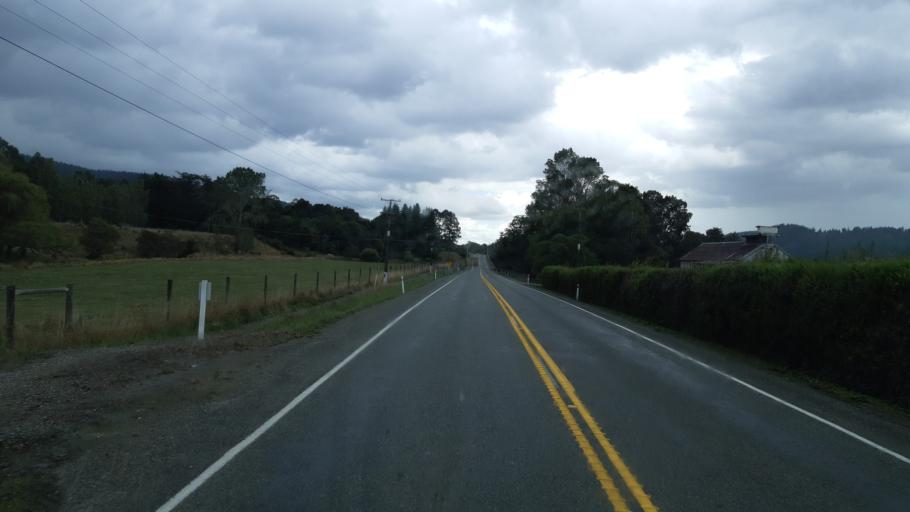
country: NZ
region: Tasman
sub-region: Tasman District
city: Wakefield
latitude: -41.4478
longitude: 172.9616
